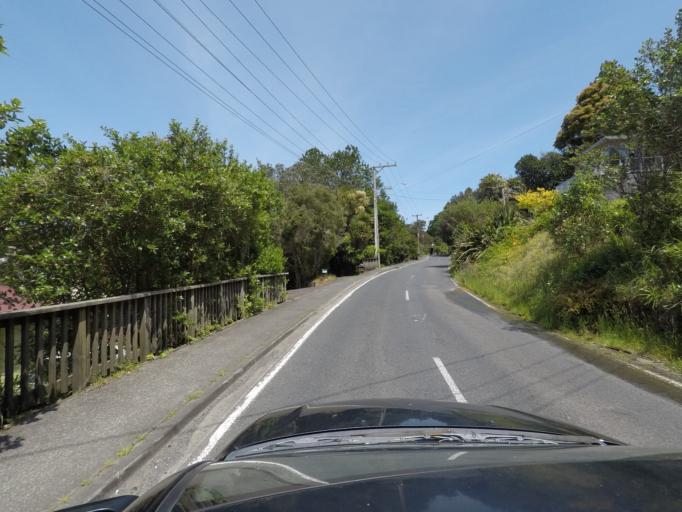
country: NZ
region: Auckland
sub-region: Auckland
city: Titirangi
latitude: -36.9645
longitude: 174.6409
